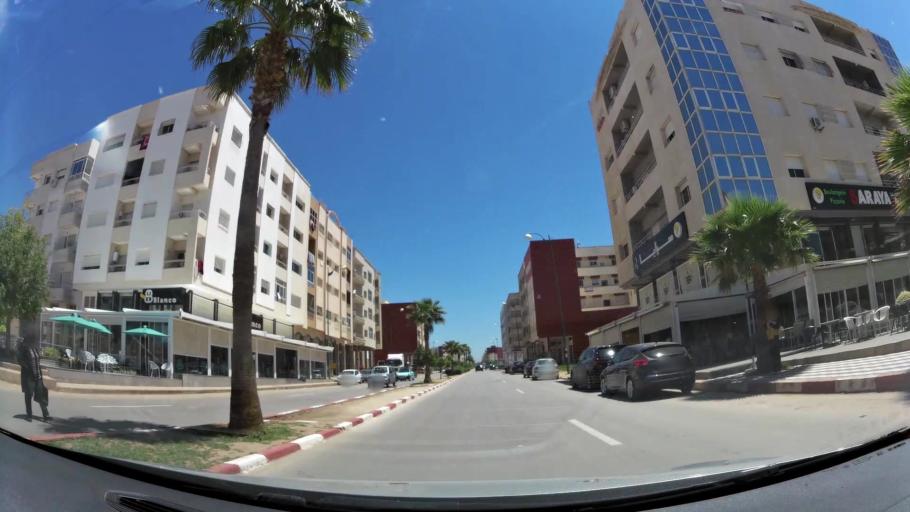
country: MA
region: Meknes-Tafilalet
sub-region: Meknes
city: Meknes
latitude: 33.8591
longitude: -5.5629
